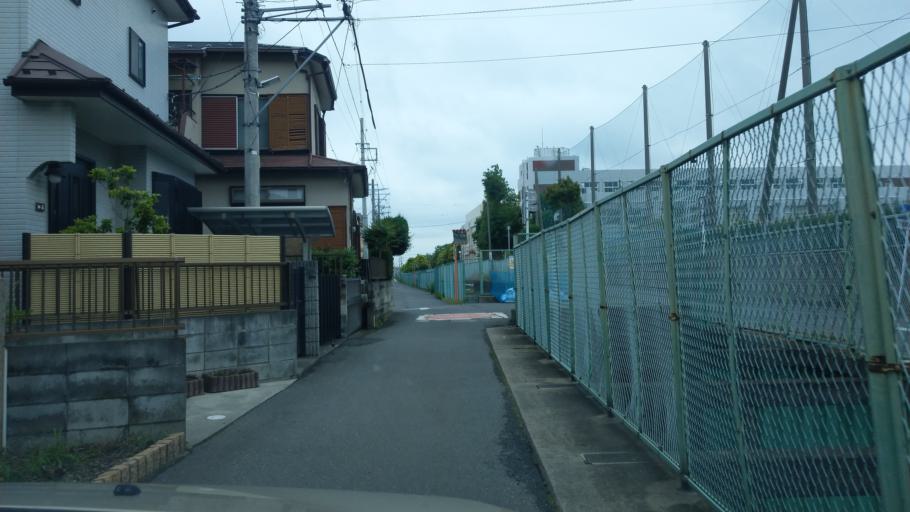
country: JP
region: Saitama
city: Yono
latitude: 35.8776
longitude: 139.6076
